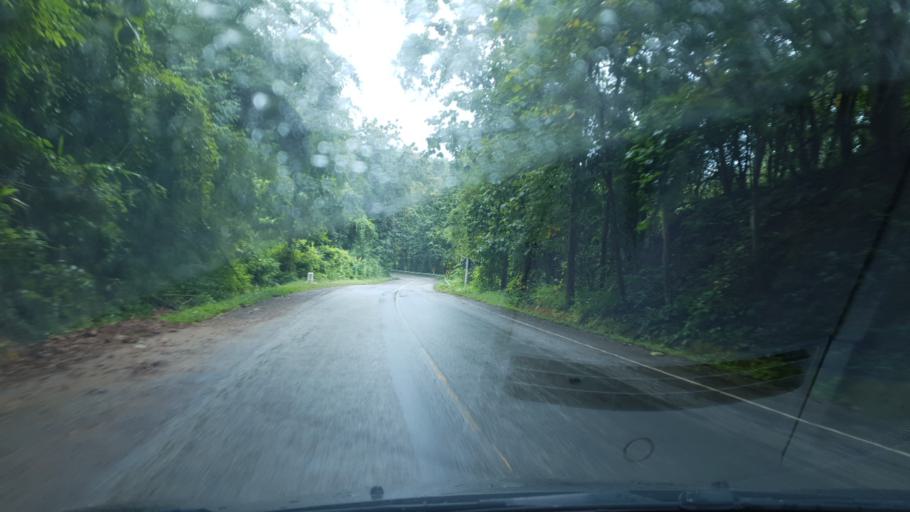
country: TH
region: Mae Hong Son
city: Pa Pae
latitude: 18.2771
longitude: 97.9393
